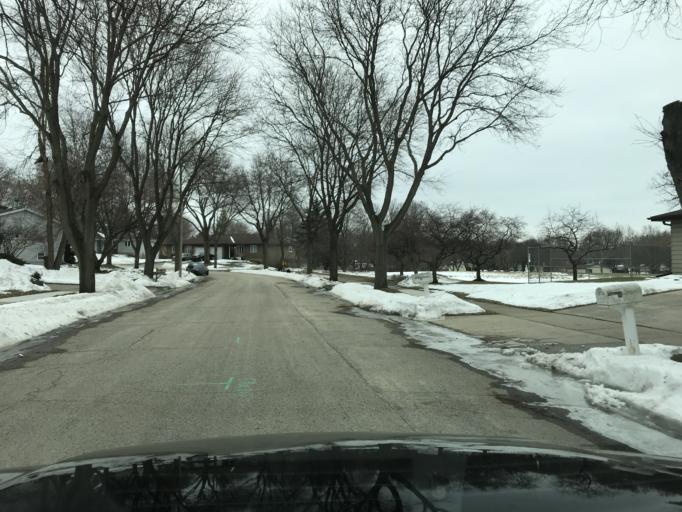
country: US
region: Wisconsin
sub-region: Dane County
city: Monona
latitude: 43.0785
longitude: -89.2844
